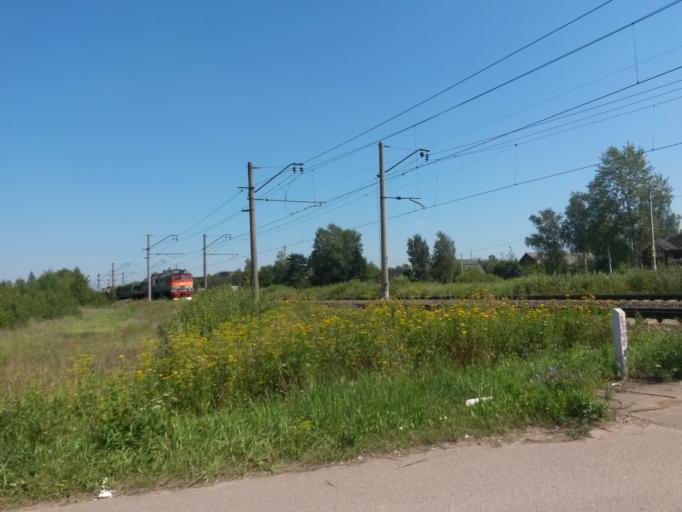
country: RU
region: Moskovskaya
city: Stolbovaya
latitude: 55.2583
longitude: 37.4820
